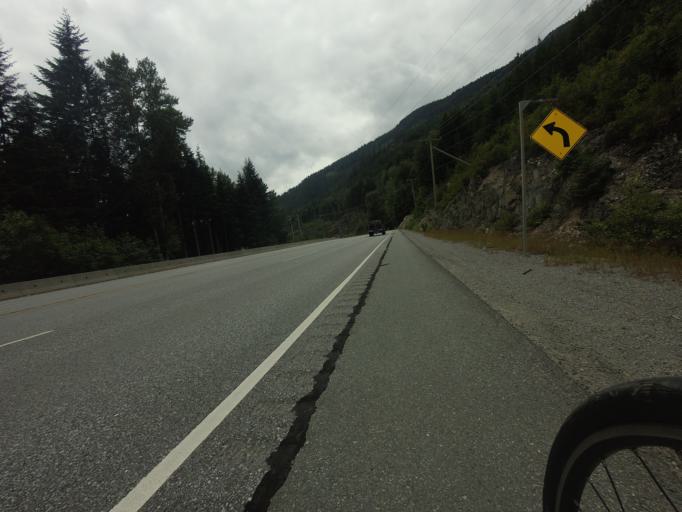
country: CA
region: British Columbia
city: Whistler
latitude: 50.0841
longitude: -123.0609
